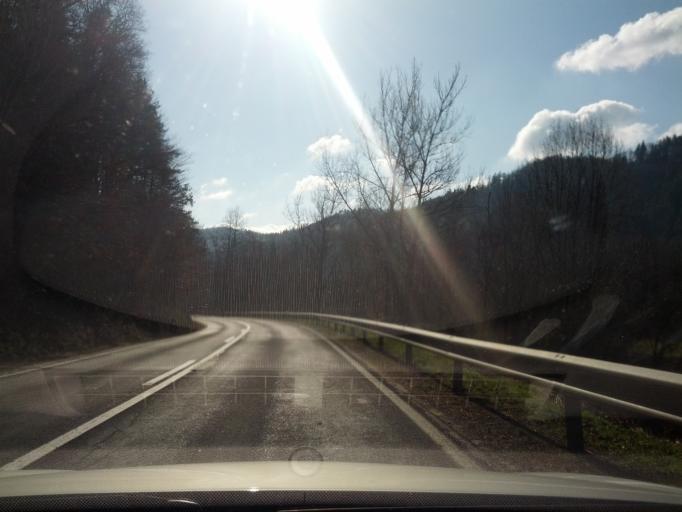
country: SI
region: Moravce
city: Moravce
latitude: 46.0930
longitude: 14.6949
